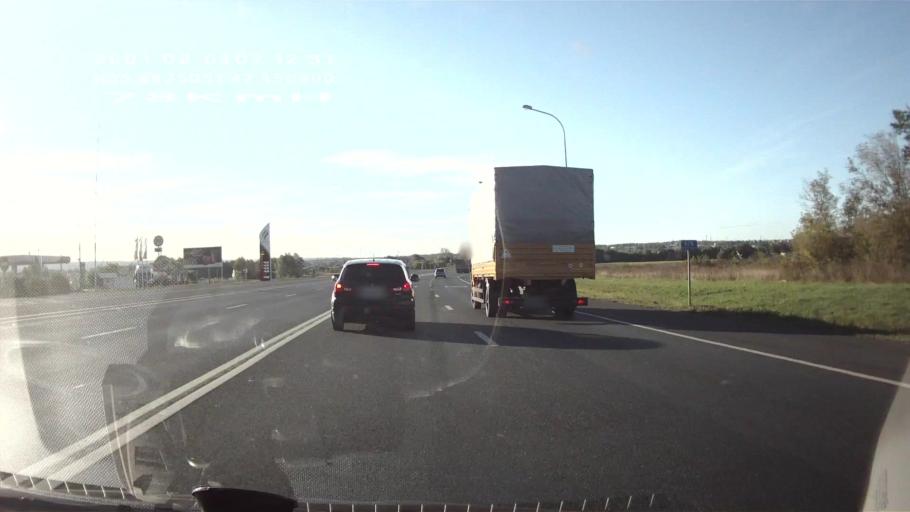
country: RU
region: Chuvashia
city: Tsivil'sk
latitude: 55.8817
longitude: 47.4501
